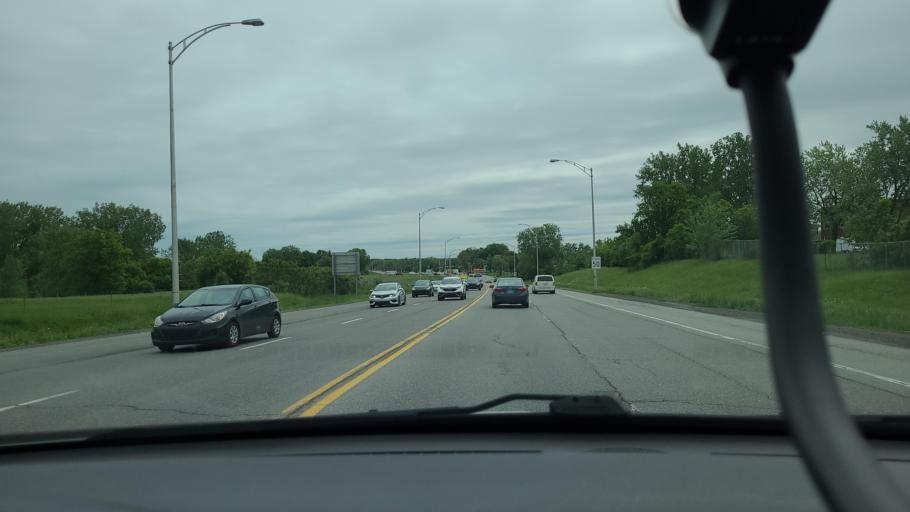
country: CA
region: Quebec
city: Bois-des-Filion
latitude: 45.6693
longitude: -73.7632
